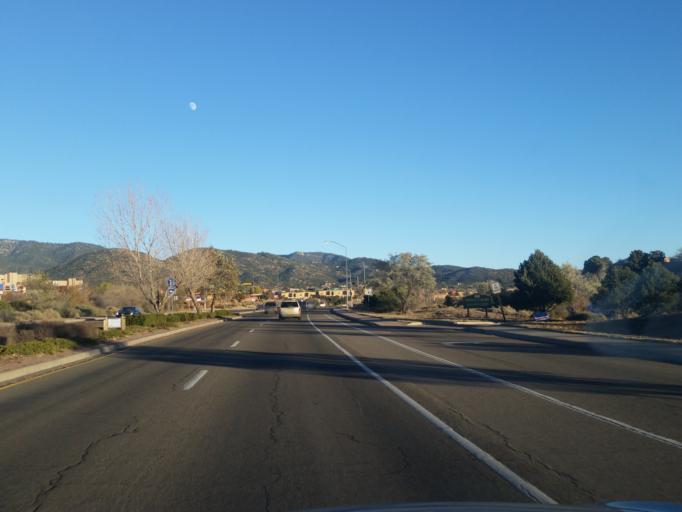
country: US
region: New Mexico
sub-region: Santa Fe County
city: Santa Fe
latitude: 35.6585
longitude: -105.9504
